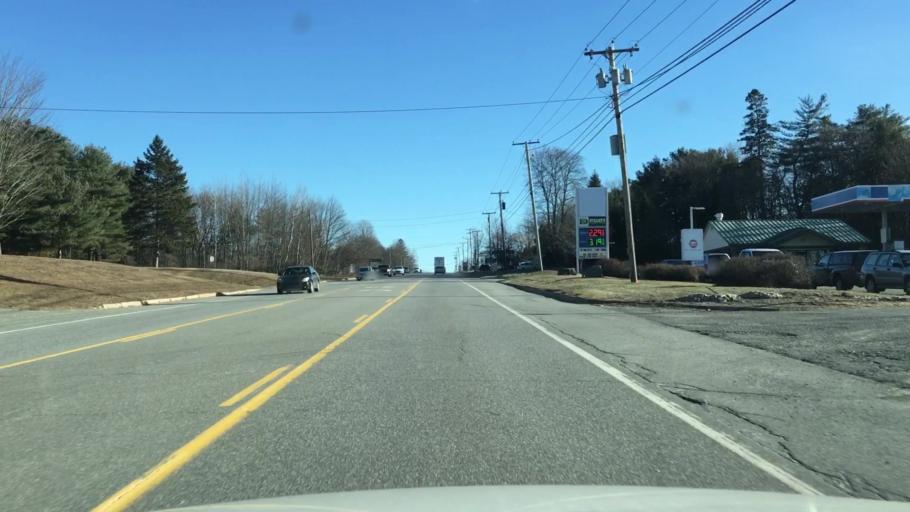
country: US
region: Maine
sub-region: Penobscot County
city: Holden
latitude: 44.7667
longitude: -68.7108
